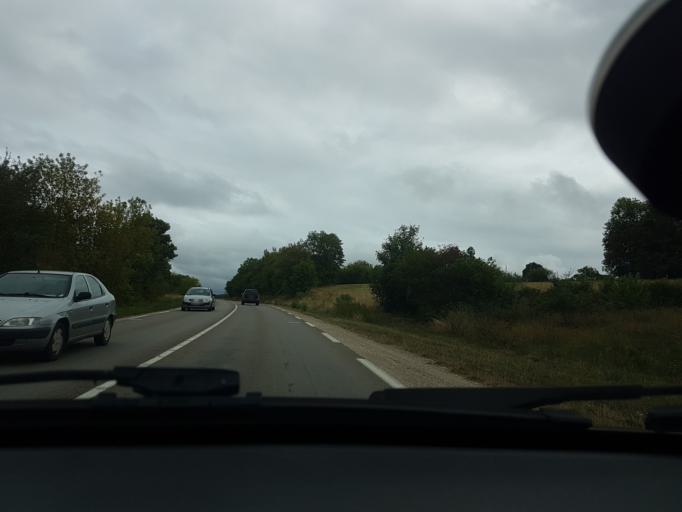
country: FR
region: Bourgogne
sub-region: Departement de l'Yonne
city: Champs-sur-Yonne
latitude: 47.6982
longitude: 3.6325
